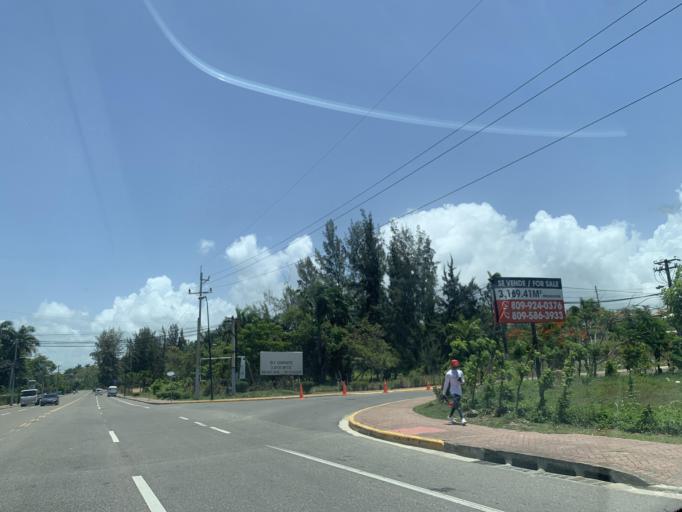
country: DO
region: Puerto Plata
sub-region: Puerto Plata
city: Puerto Plata
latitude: 19.7763
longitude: -70.6601
